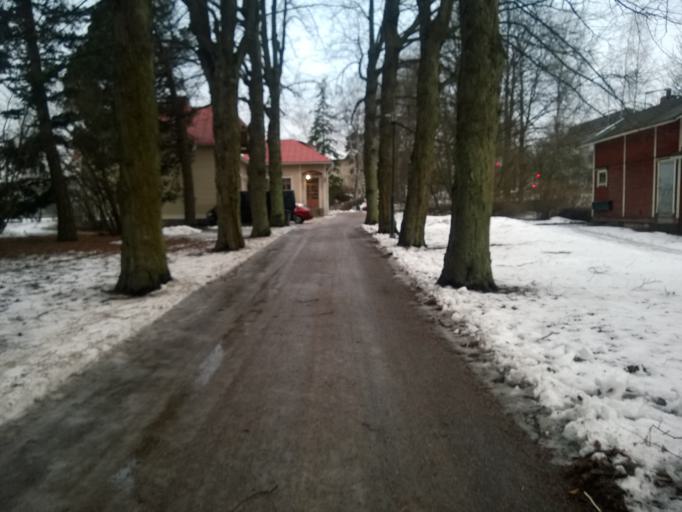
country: FI
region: Uusimaa
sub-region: Helsinki
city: Teekkarikylae
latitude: 60.2235
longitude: 24.8613
